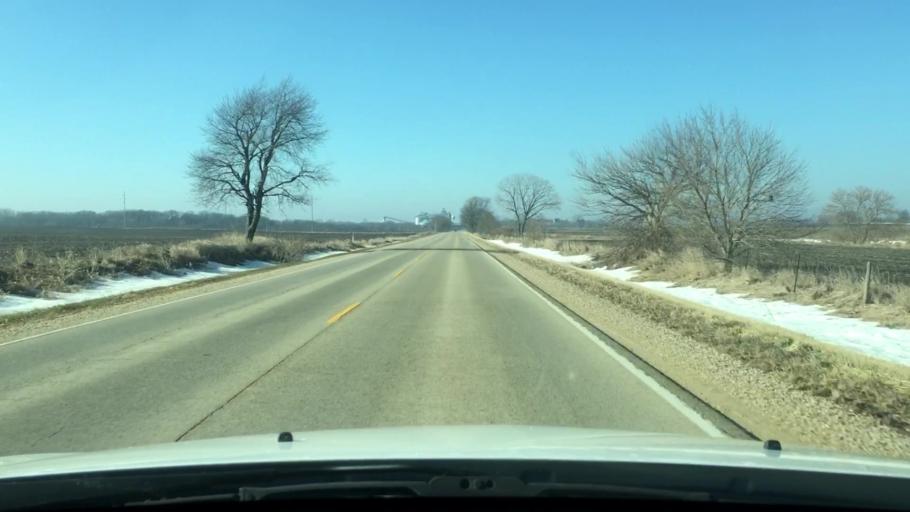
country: US
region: Illinois
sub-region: Ogle County
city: Rochelle
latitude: 41.8478
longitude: -88.9934
